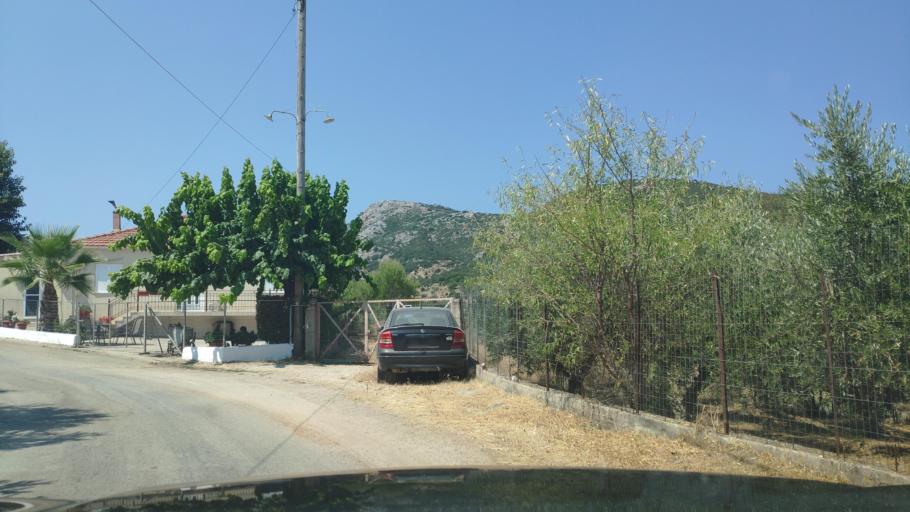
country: GR
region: West Greece
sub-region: Nomos Aitolias kai Akarnanias
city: Monastirakion
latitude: 38.8473
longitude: 20.9445
